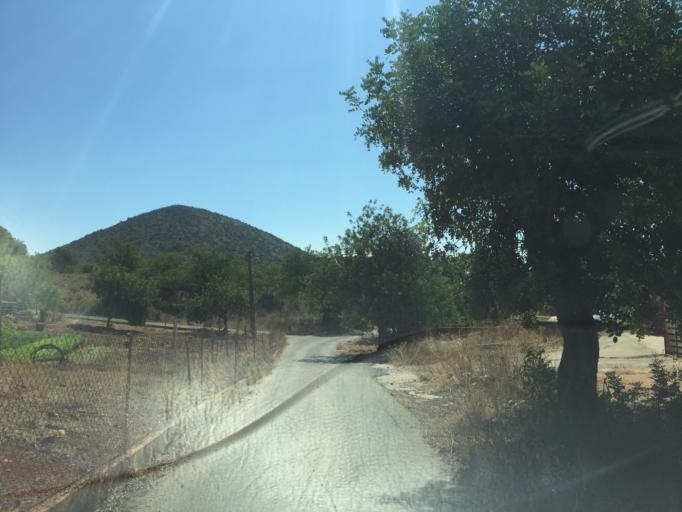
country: PT
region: Faro
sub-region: Loule
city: Vilamoura
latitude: 37.1170
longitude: -8.0814
